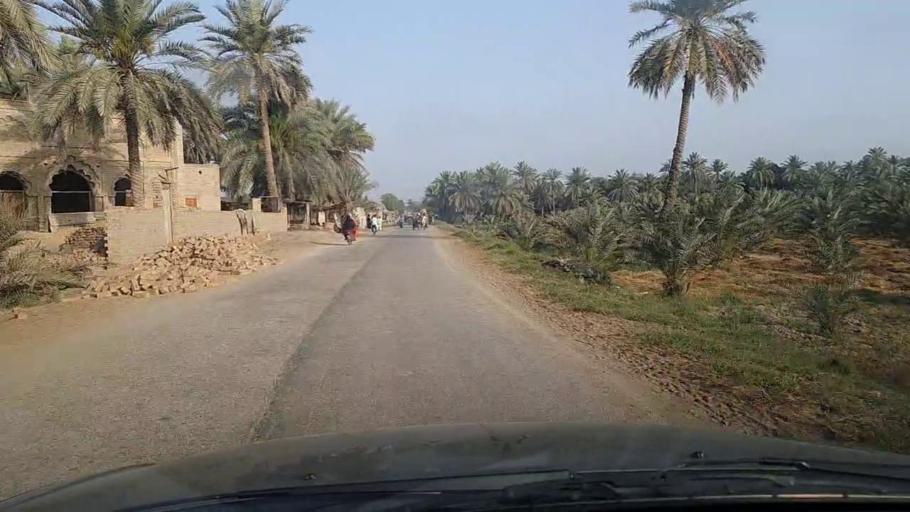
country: PK
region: Sindh
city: Pir jo Goth
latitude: 27.5561
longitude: 68.6771
